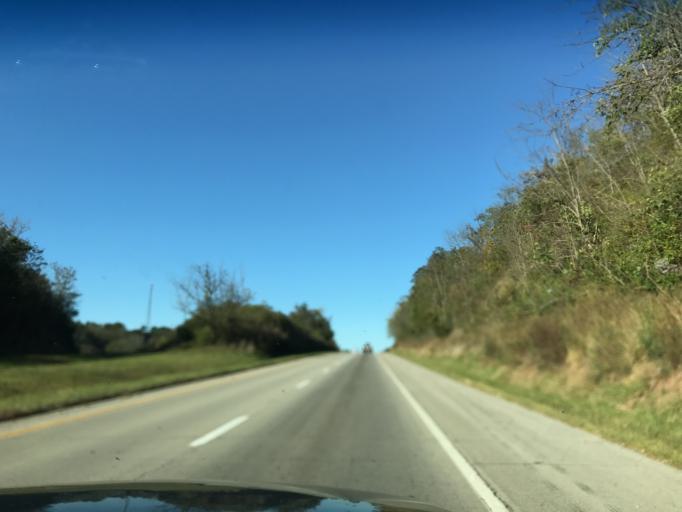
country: US
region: West Virginia
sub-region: Wood County
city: Washington
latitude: 39.2853
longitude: -81.6672
